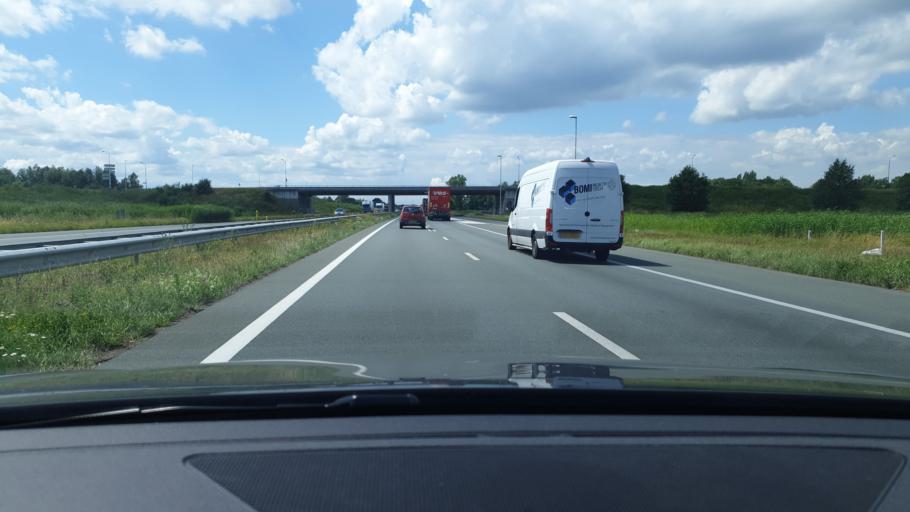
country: NL
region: North Brabant
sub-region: Gemeente Veghel
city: Mariaheide
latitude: 51.6381
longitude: 5.5709
